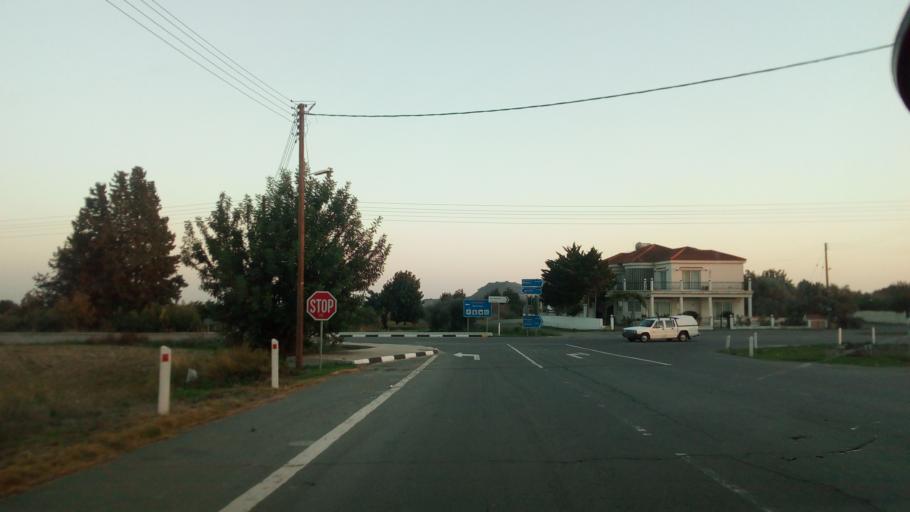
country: CY
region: Larnaka
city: Kofinou
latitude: 34.8514
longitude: 33.4509
